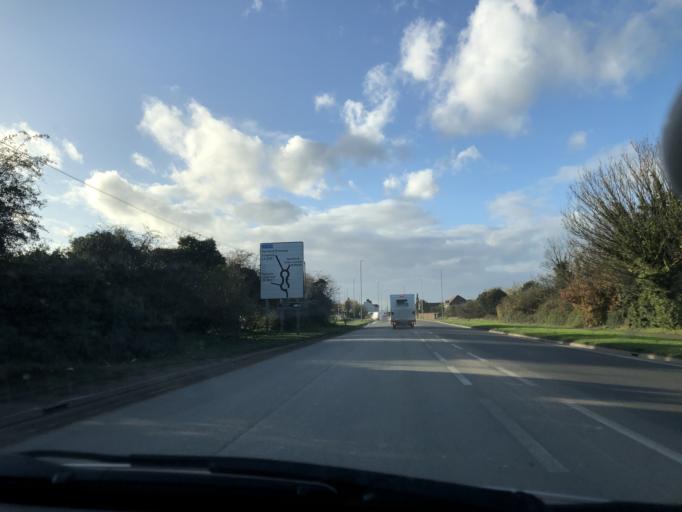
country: GB
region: England
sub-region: Kent
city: Stone
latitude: 51.4377
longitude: 0.2578
